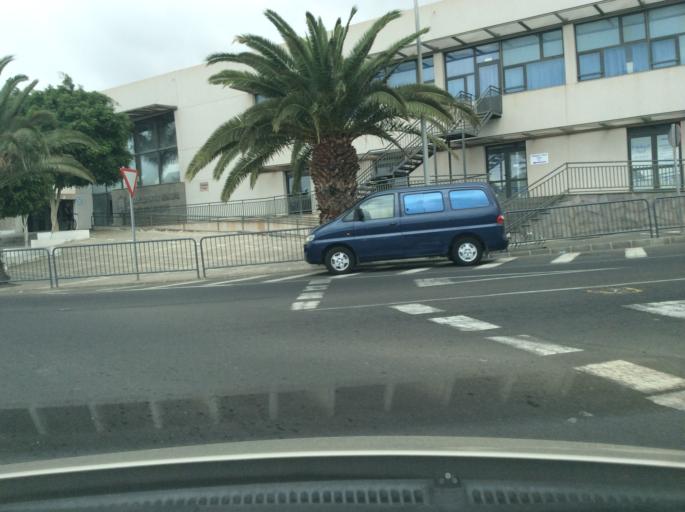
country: ES
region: Canary Islands
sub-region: Provincia de Las Palmas
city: Arrecife
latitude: 28.9689
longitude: -13.5471
